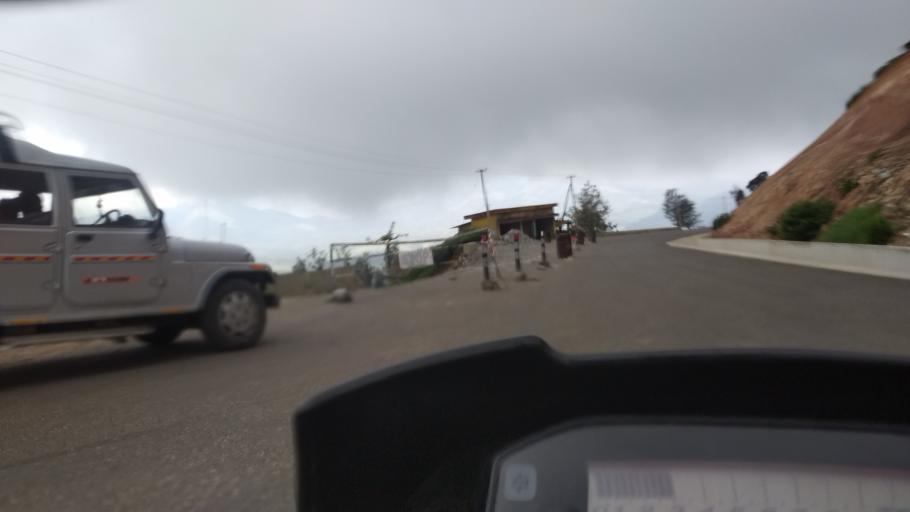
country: IN
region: Kerala
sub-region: Idukki
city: Munnar
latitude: 10.0349
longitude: 77.1588
